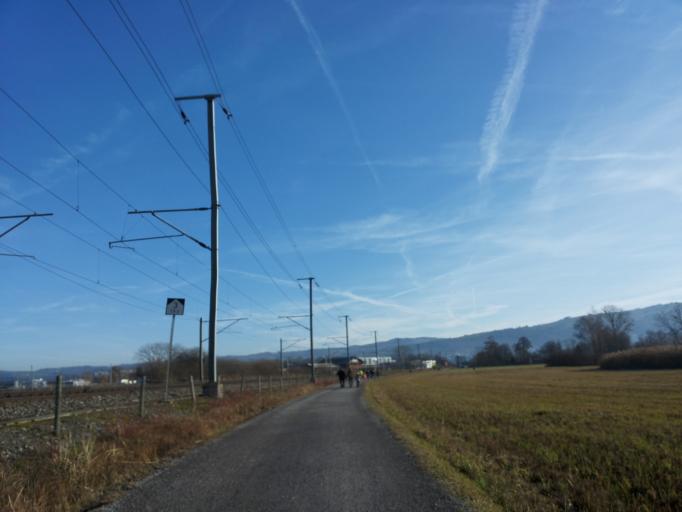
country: CH
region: Zug
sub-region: Zug
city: Cham
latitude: 47.1829
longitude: 8.4769
